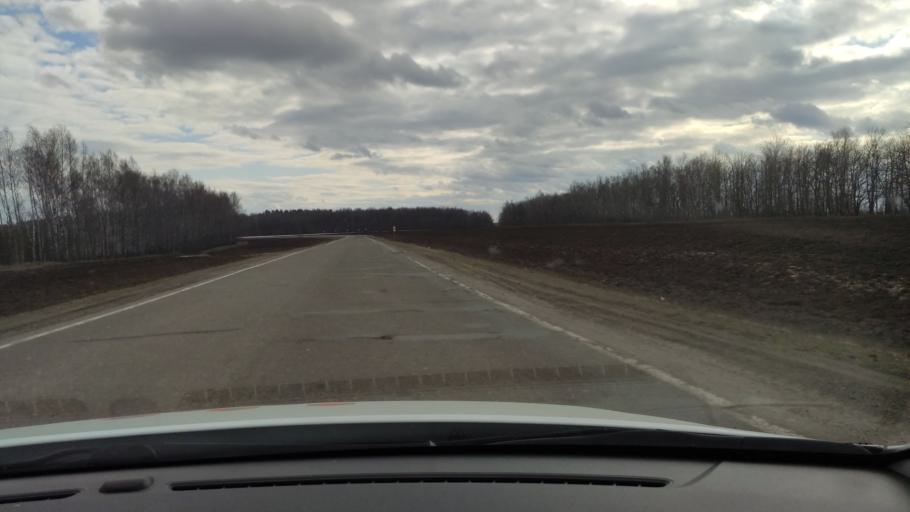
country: RU
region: Tatarstan
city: Vysokaya Gora
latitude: 56.0901
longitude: 49.1807
